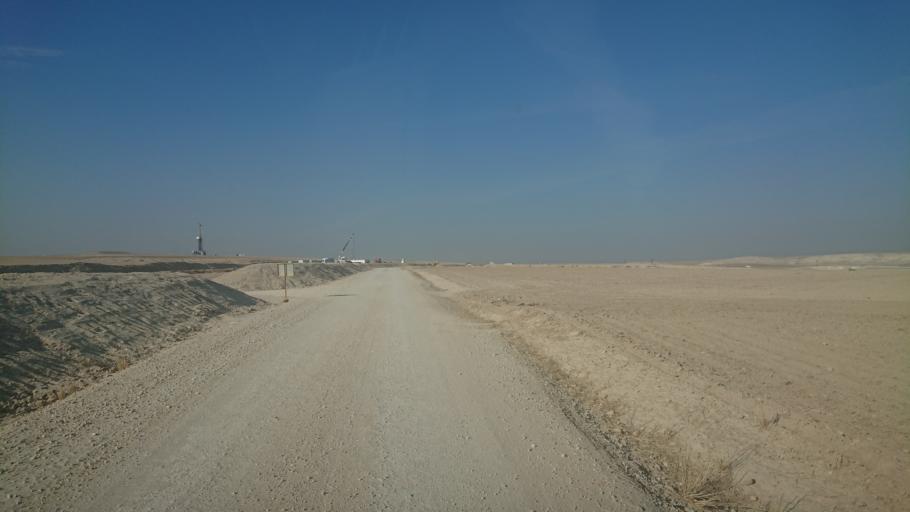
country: TR
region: Aksaray
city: Sultanhani
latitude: 38.0704
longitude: 33.6142
